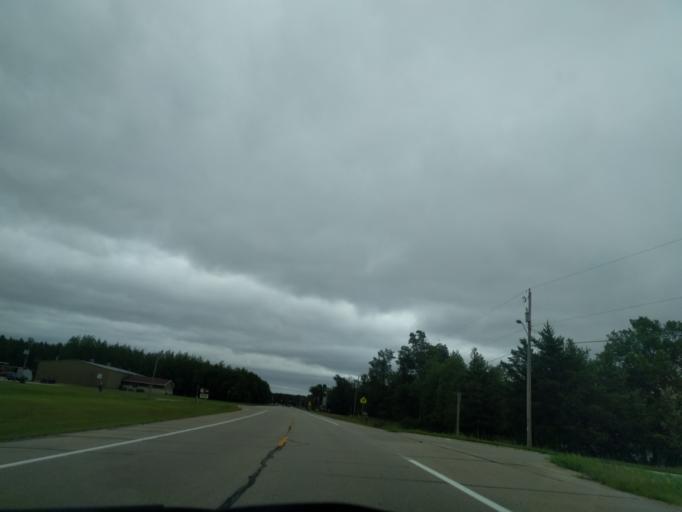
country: US
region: Michigan
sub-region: Delta County
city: Gladstone
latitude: 45.8553
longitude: -87.0564
